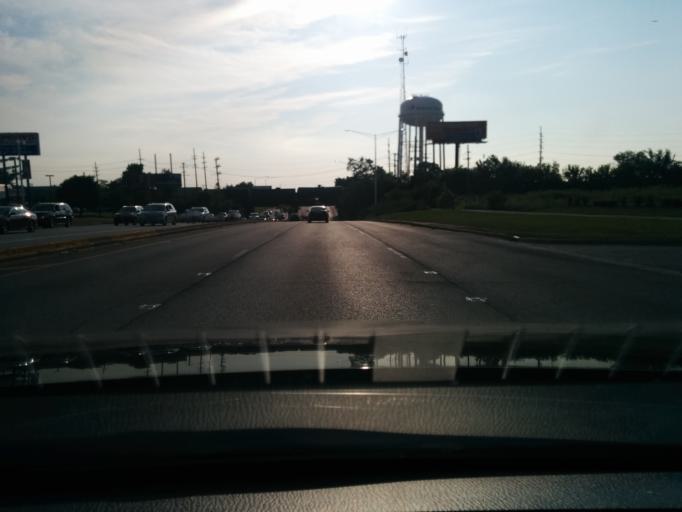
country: US
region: Illinois
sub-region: Cook County
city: Melrose Park
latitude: 41.9078
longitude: -87.8663
